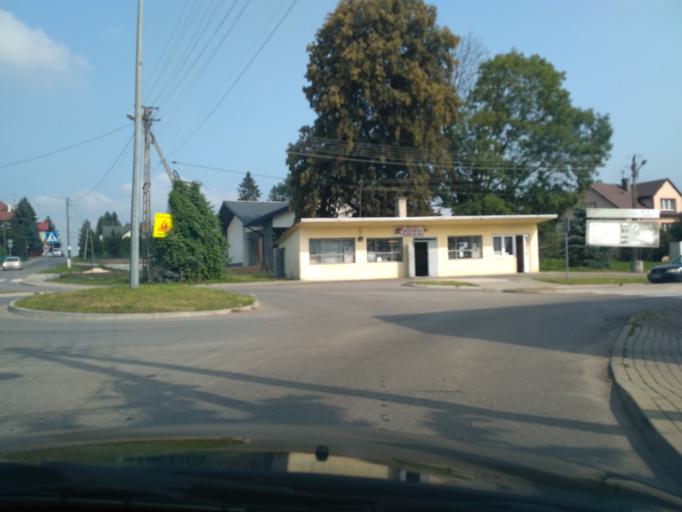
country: PL
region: Subcarpathian Voivodeship
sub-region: Powiat rzeszowski
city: Niechobrz
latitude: 49.9942
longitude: 21.8760
